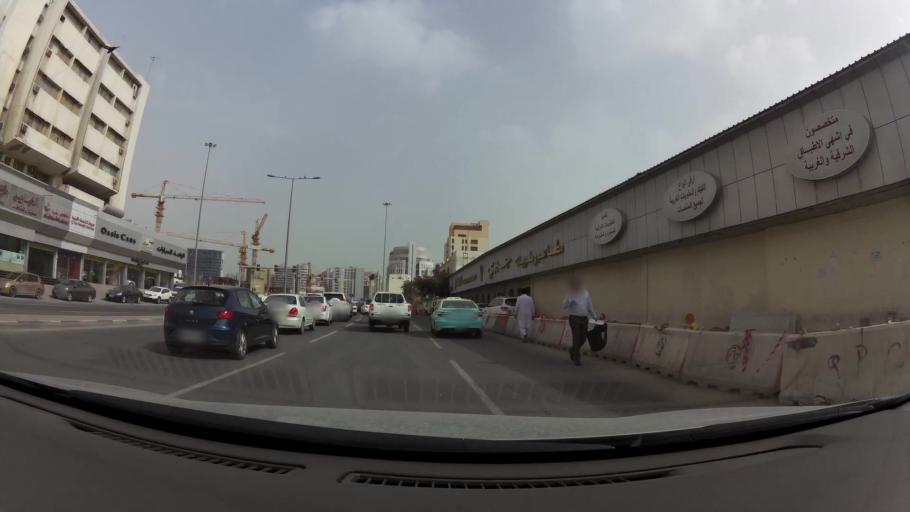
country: QA
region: Baladiyat ad Dawhah
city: Doha
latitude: 25.2819
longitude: 51.5446
